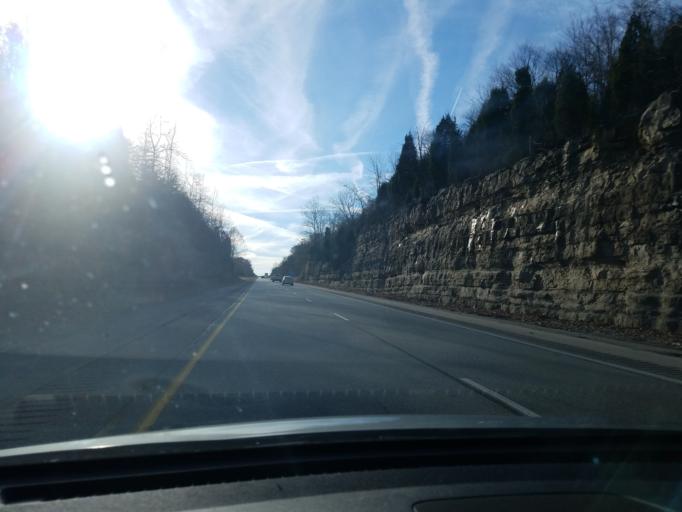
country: US
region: Indiana
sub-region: Floyd County
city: Georgetown
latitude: 38.2825
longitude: -85.9440
